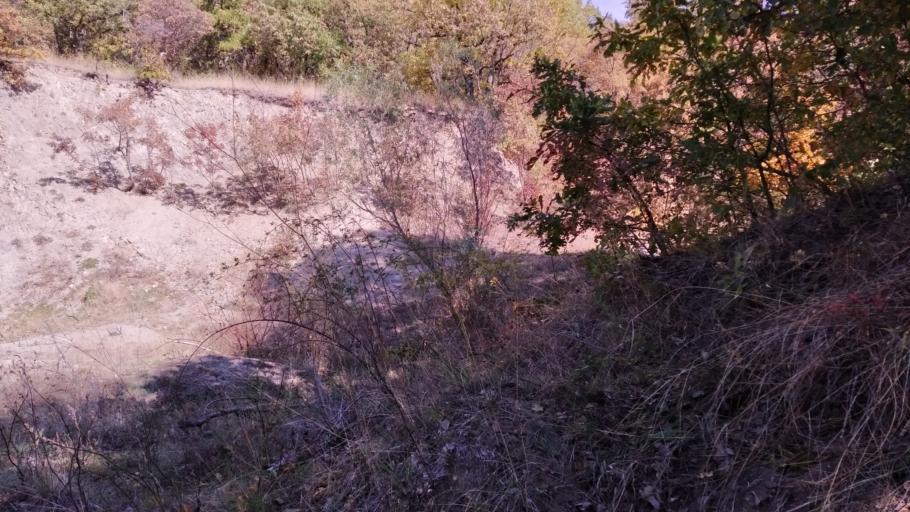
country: HU
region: Pest
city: Visegrad
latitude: 47.7359
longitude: 18.9734
